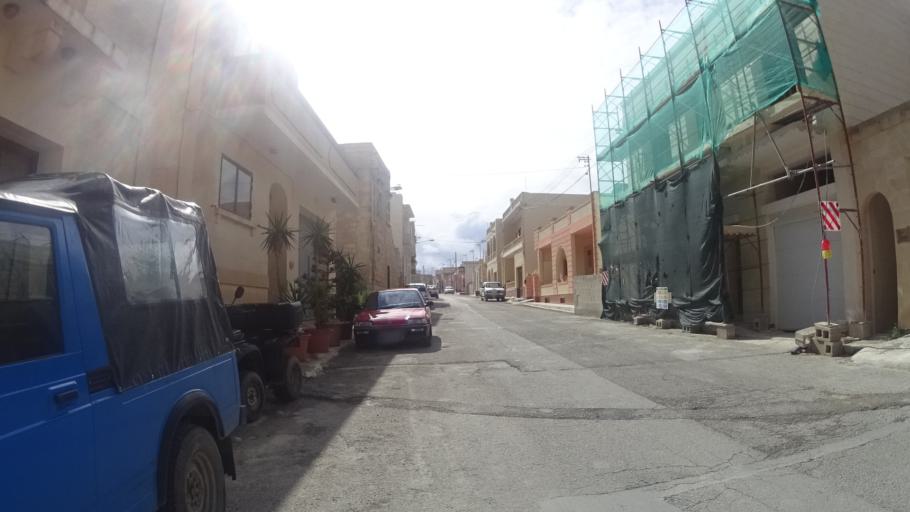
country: MT
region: In-Nadur
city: Nadur
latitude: 36.0465
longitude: 14.2995
